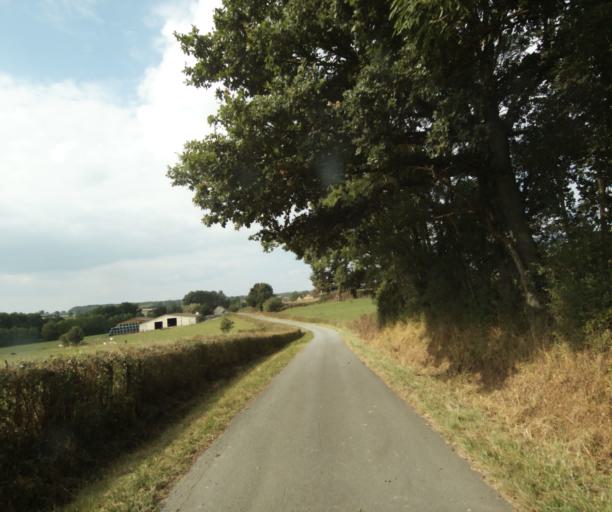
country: FR
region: Bourgogne
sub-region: Departement de Saone-et-Loire
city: Palinges
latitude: 46.5033
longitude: 4.1891
